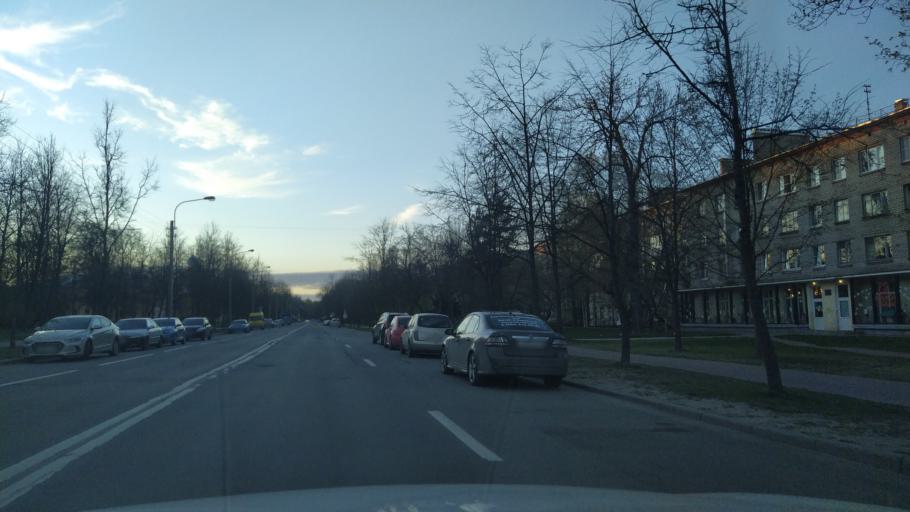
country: RU
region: St.-Petersburg
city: Pushkin
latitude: 59.7041
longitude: 30.4068
